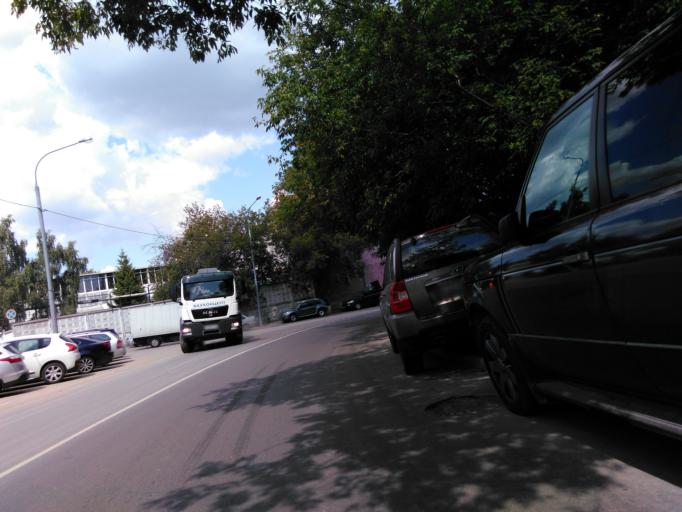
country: RU
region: Moscow
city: Kotlovka
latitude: 55.6865
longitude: 37.6124
